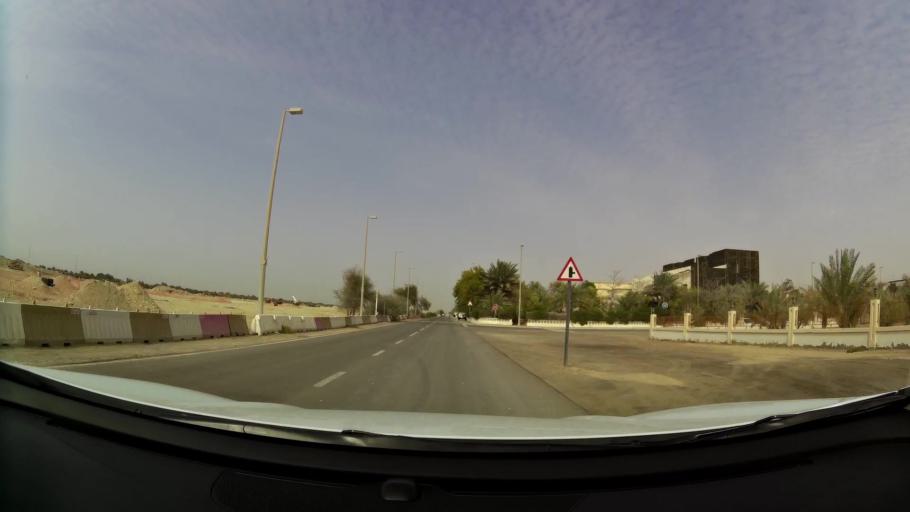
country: AE
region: Abu Dhabi
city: Abu Dhabi
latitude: 24.5977
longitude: 54.6956
